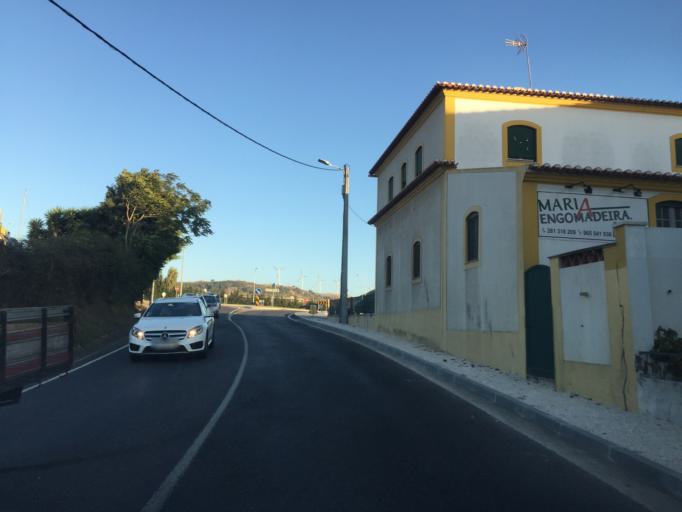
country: PT
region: Lisbon
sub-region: Torres Vedras
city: Torres Vedras
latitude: 39.0726
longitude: -9.2493
